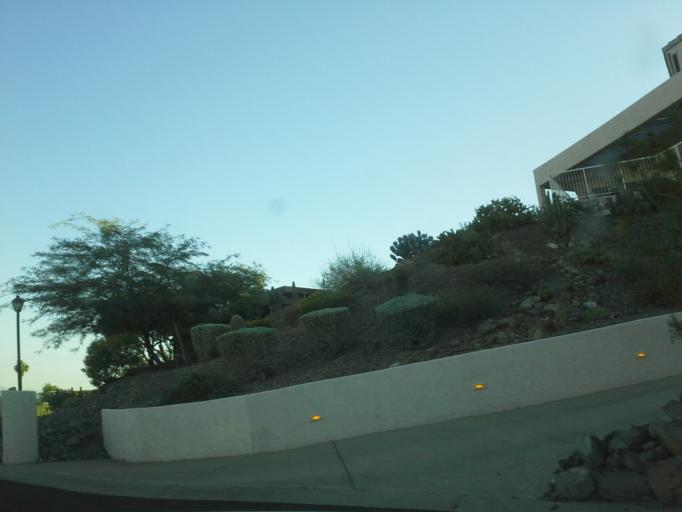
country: US
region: Arizona
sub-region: Maricopa County
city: Glendale
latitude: 33.6044
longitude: -112.0861
